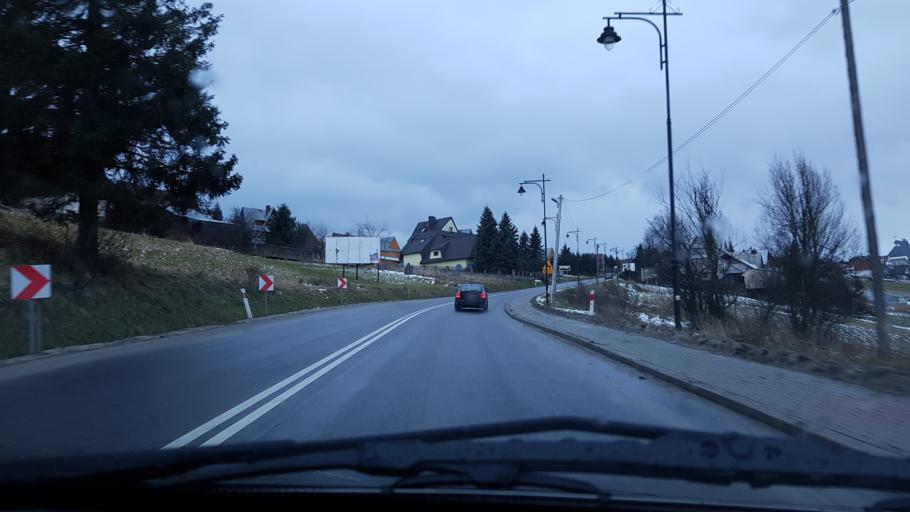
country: PL
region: Lesser Poland Voivodeship
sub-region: Powiat tatrzanski
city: Bukowina Tatrzanska
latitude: 49.3480
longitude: 20.1166
